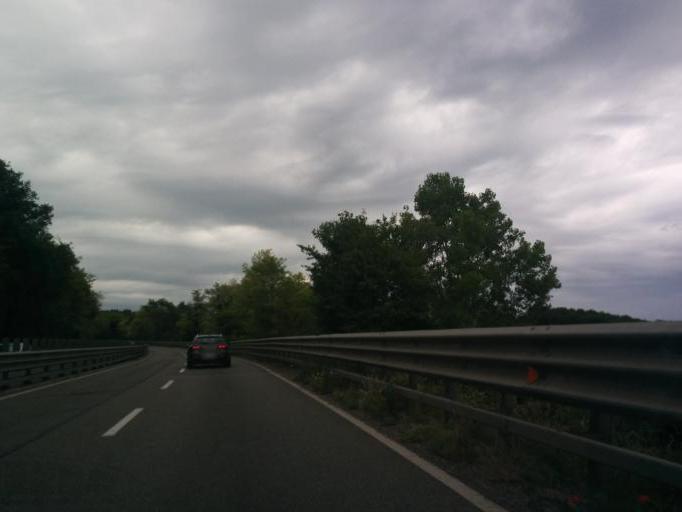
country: IT
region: Tuscany
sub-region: Provincia di Siena
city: Belverde
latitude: 43.3718
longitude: 11.2873
